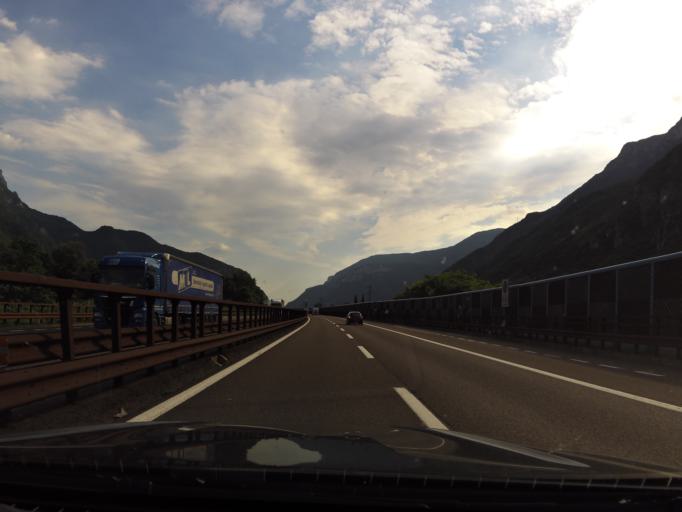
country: IT
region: Trentino-Alto Adige
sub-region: Provincia di Trento
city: Avio
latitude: 45.7115
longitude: 10.9281
